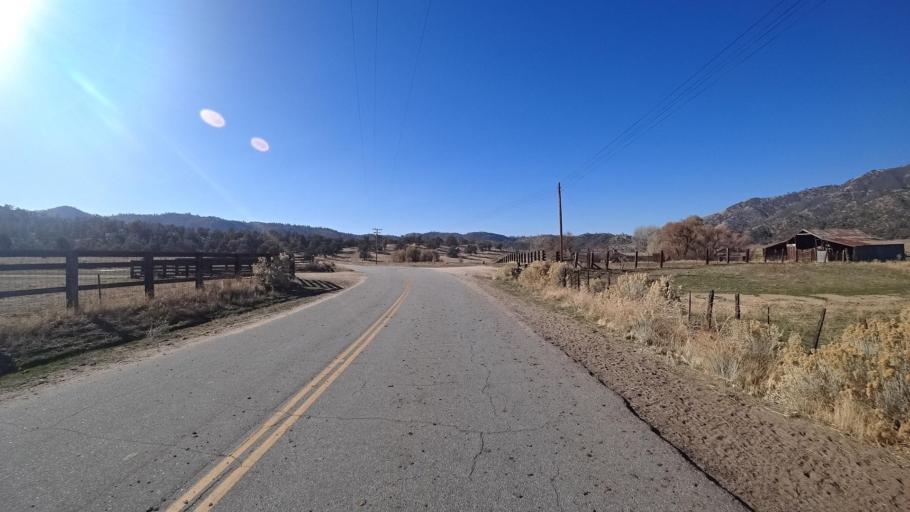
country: US
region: California
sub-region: Kern County
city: Bodfish
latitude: 35.3892
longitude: -118.5340
